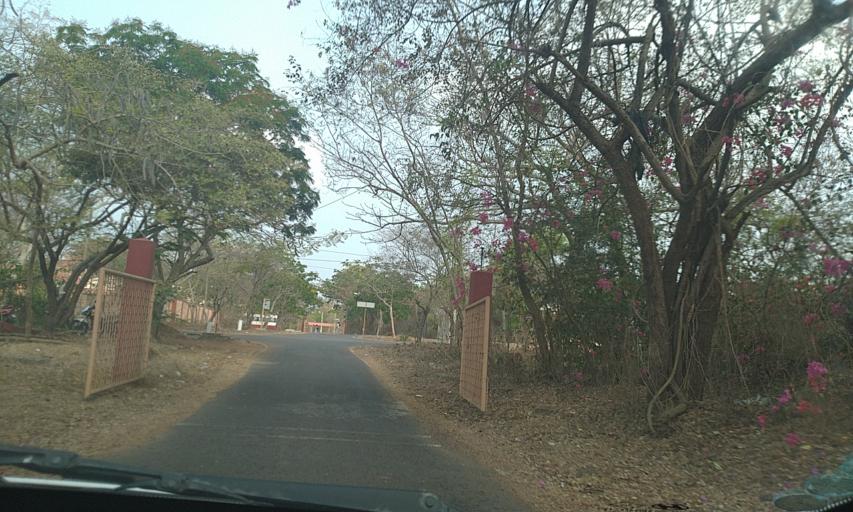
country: IN
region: Goa
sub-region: North Goa
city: Taleigao
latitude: 15.4557
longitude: 73.8353
